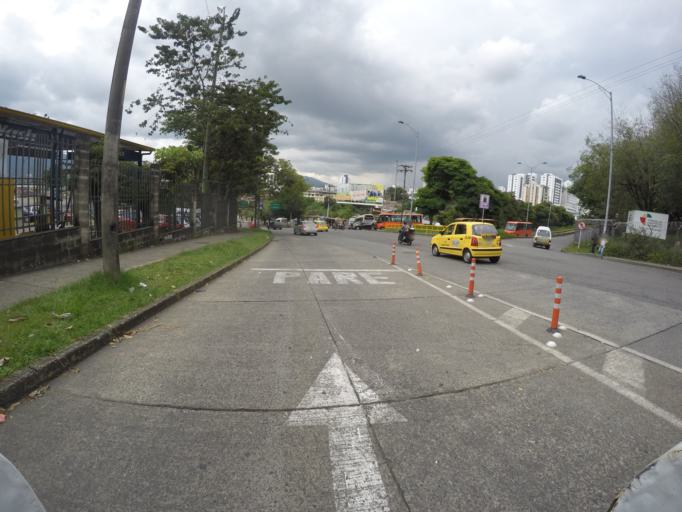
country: CO
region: Risaralda
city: Pereira
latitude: 4.8026
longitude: -75.6940
